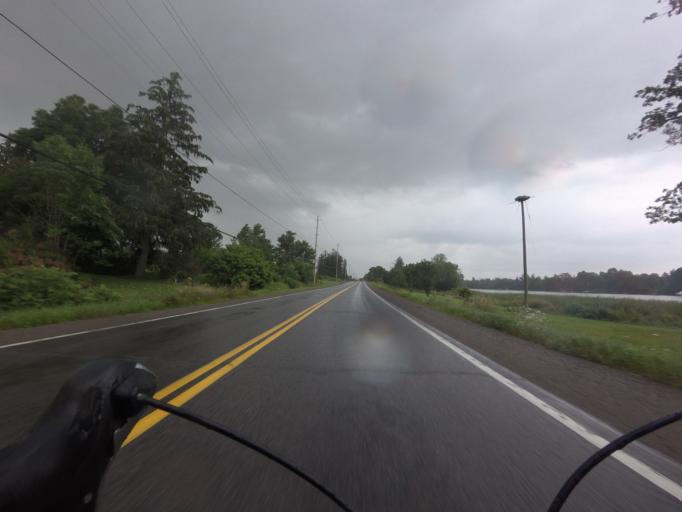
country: CA
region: Ontario
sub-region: Lanark County
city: Smiths Falls
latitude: 44.9411
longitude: -75.8278
